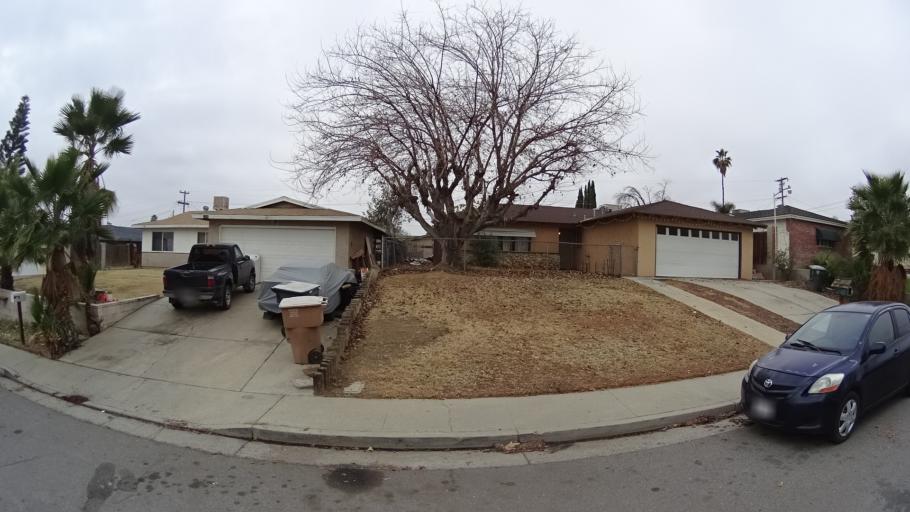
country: US
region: California
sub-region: Kern County
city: Bakersfield
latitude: 35.3826
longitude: -118.9263
